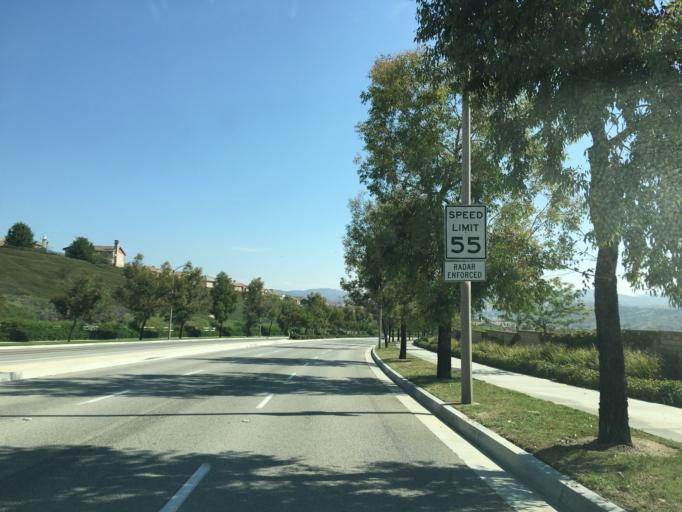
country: US
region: California
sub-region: Los Angeles County
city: Valencia
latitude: 34.4584
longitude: -118.5658
